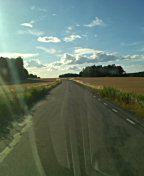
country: SE
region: Uppsala
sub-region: Habo Kommun
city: Balsta
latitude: 59.6667
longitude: 17.5529
